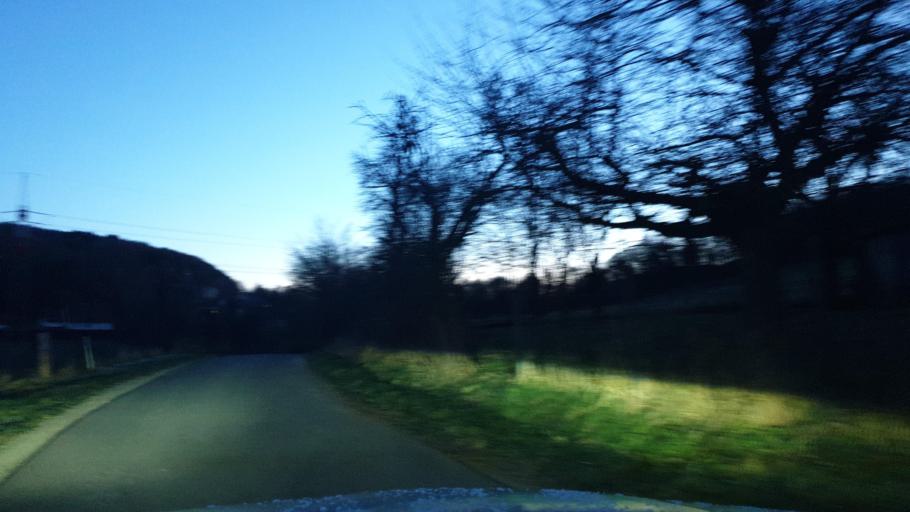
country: DE
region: North Rhine-Westphalia
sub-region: Regierungsbezirk Detmold
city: Hille
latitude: 52.2785
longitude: 8.7562
